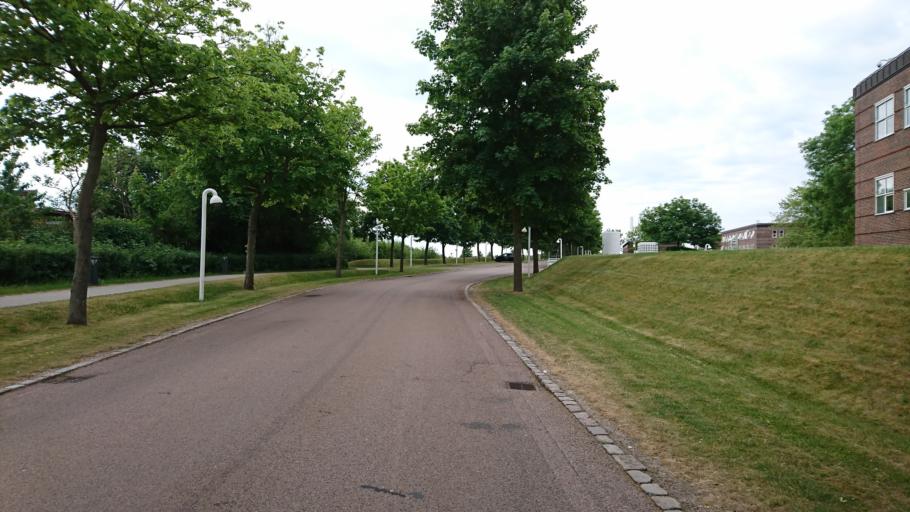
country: DK
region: Capital Region
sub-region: Ballerup Kommune
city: Ballerup
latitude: 55.7381
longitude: 12.4000
